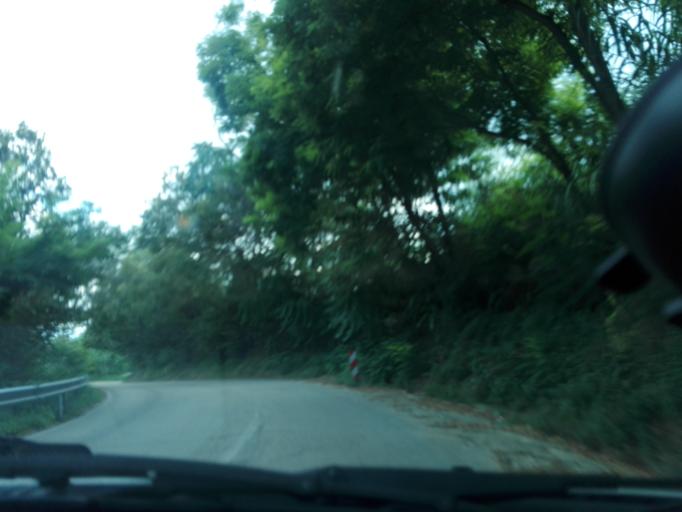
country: IT
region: Abruzzo
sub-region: Provincia di Pescara
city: Spoltore
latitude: 42.4753
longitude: 14.1364
